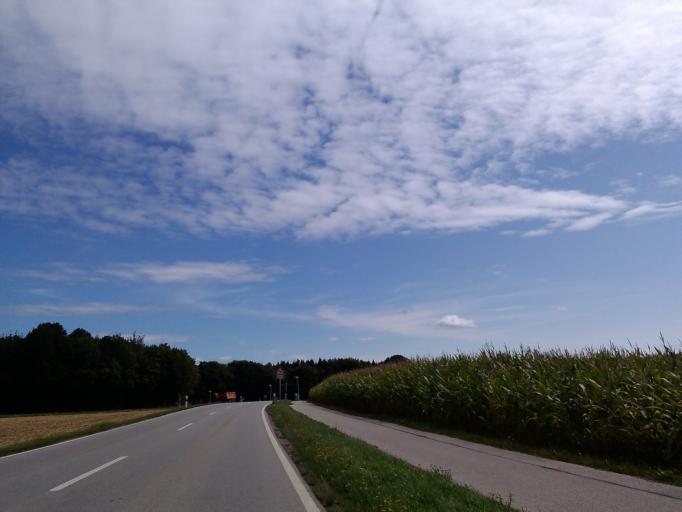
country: DE
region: Bavaria
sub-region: Upper Bavaria
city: Gauting
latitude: 48.0694
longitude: 11.3396
